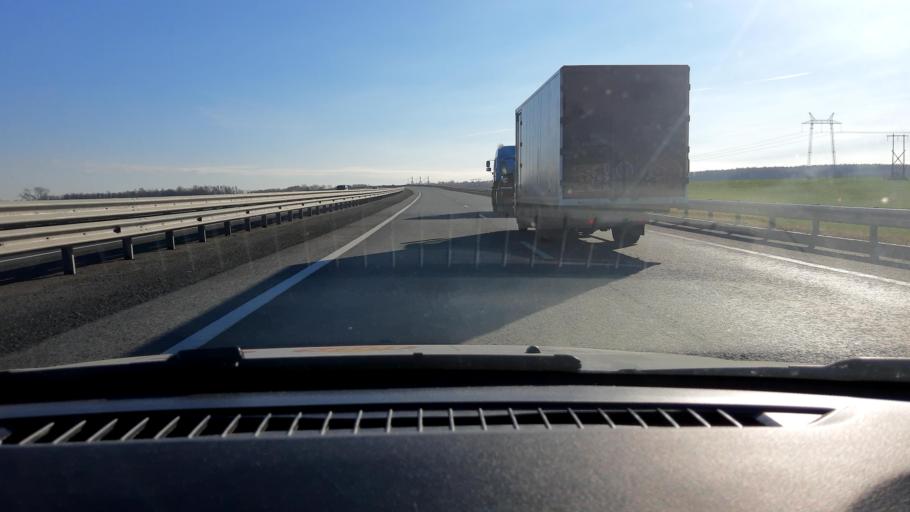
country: RU
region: Nizjnij Novgorod
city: Burevestnik
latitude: 56.1177
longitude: 43.8191
